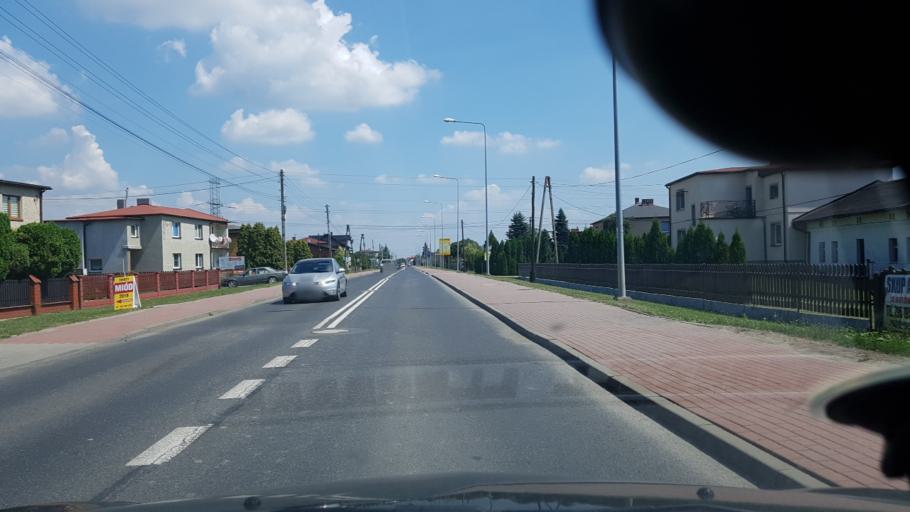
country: PL
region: Silesian Voivodeship
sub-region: Zory
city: Zory
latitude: 50.0363
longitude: 18.6614
